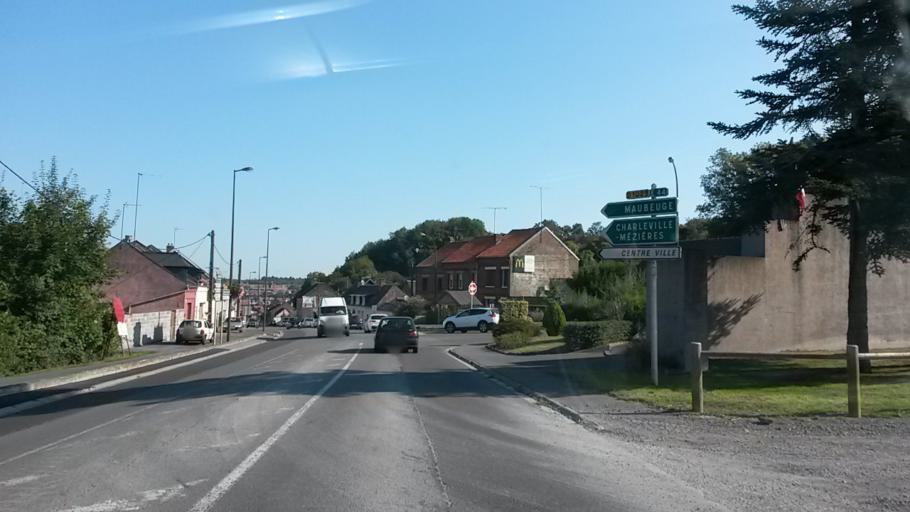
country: FR
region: Picardie
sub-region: Departement de l'Aisne
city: Guise
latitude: 49.8912
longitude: 3.6249
